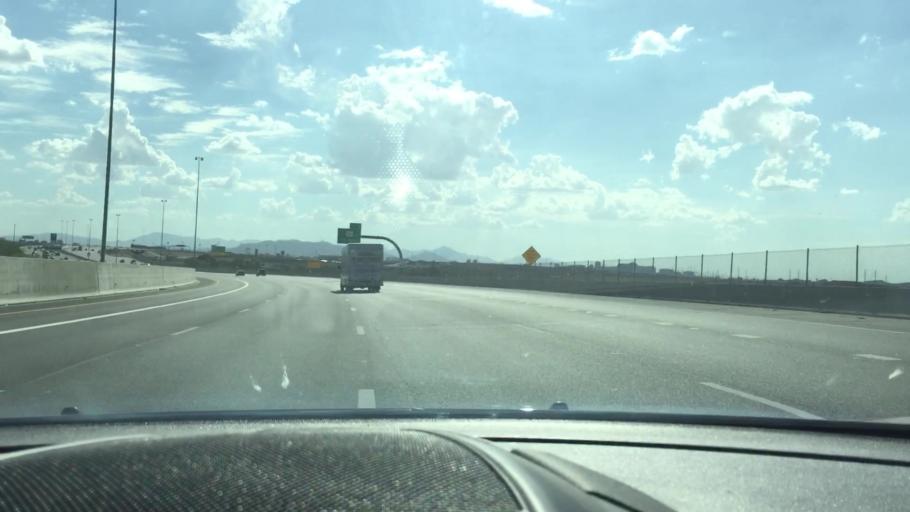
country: US
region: Arizona
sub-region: Maricopa County
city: Mesa
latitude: 33.4445
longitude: -111.8621
